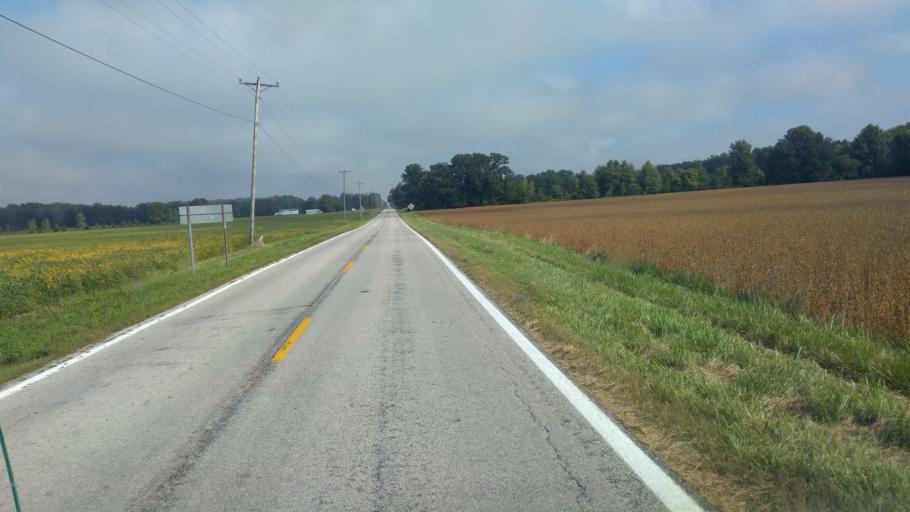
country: US
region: Ohio
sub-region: Morrow County
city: Cardington
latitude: 40.5263
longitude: -82.9626
